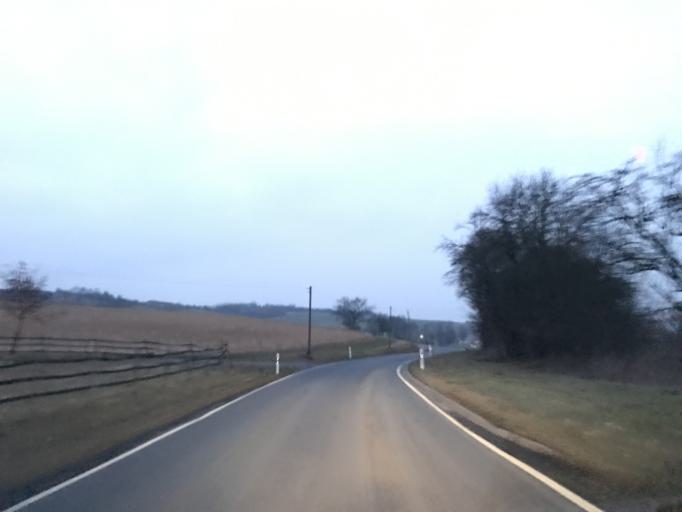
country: DE
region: Hesse
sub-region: Regierungsbezirk Kassel
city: Hofgeismar
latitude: 51.5288
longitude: 9.3851
